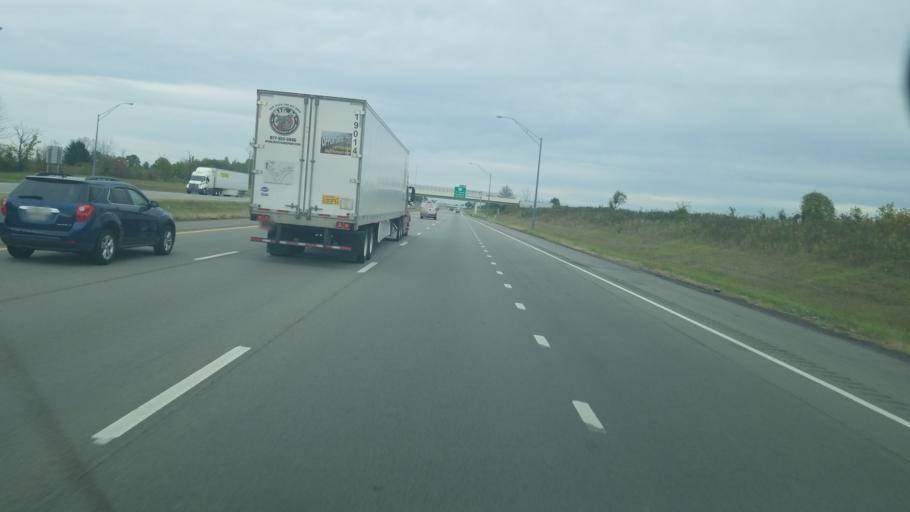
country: US
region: Ohio
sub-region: Wayne County
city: West Salem
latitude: 40.9427
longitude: -82.0941
